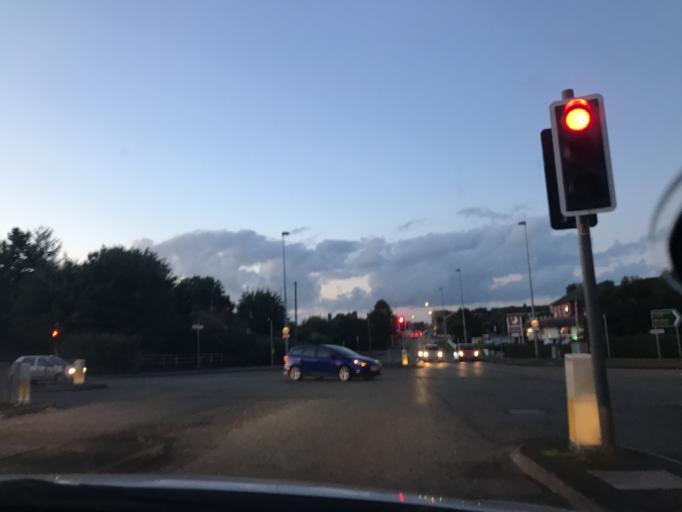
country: GB
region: England
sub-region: Cheshire West and Chester
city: Northwich
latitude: 53.2400
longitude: -2.5131
